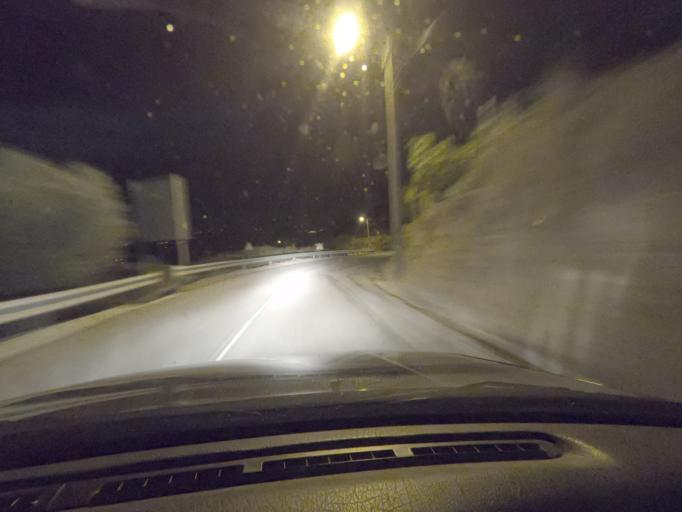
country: PT
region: Vila Real
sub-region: Santa Marta de Penaguiao
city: Santa Marta de Penaguiao
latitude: 41.2243
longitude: -7.8186
